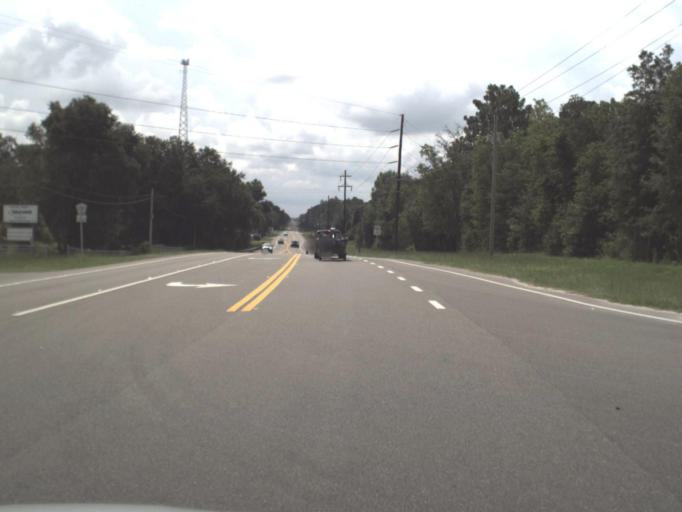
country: US
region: Florida
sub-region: Clay County
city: Keystone Heights
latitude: 29.8047
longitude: -82.0623
